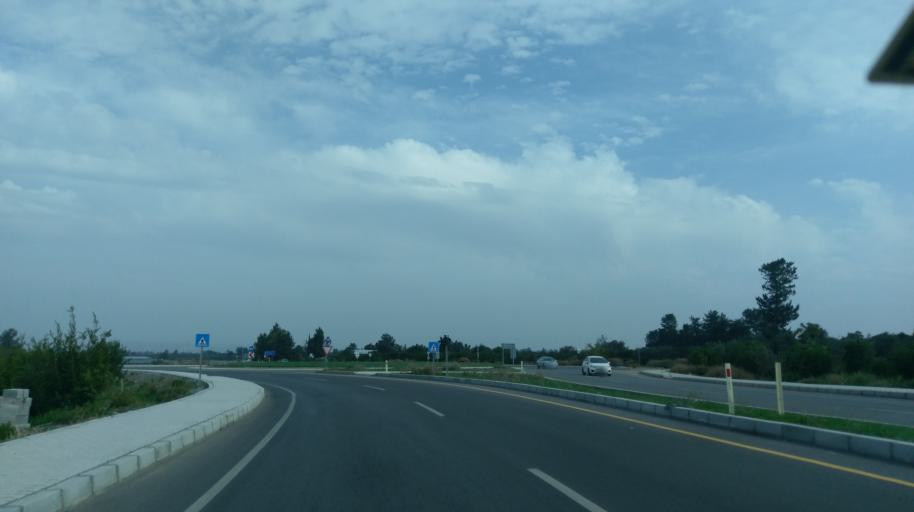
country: CY
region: Lefkosia
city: Morfou
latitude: 35.1729
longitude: 32.9563
